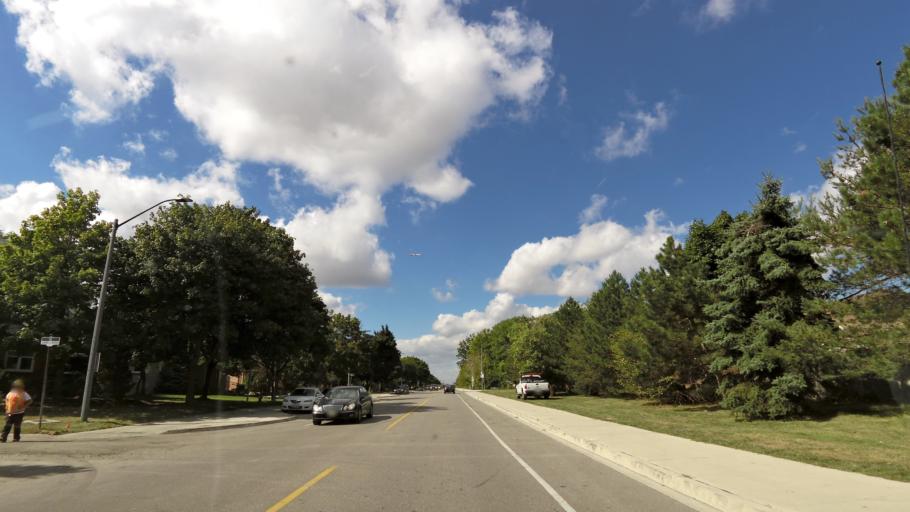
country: CA
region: Ontario
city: Mississauga
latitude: 43.5752
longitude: -79.7644
